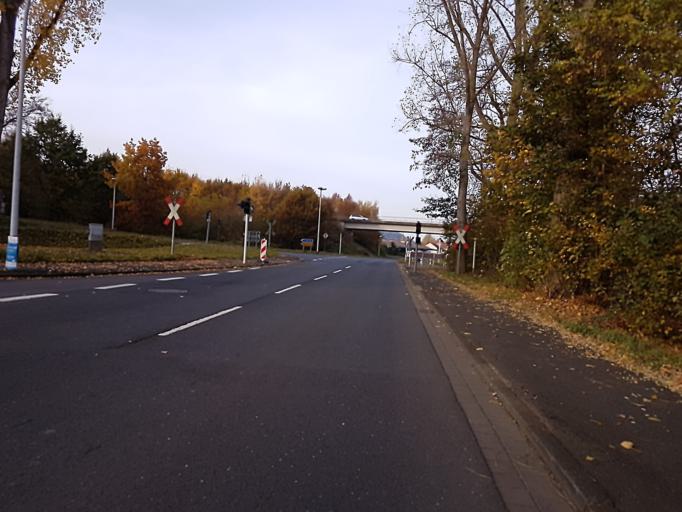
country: DE
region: Bavaria
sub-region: Regierungsbezirk Unterfranken
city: Elsenfeld
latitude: 49.8360
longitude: 9.1523
